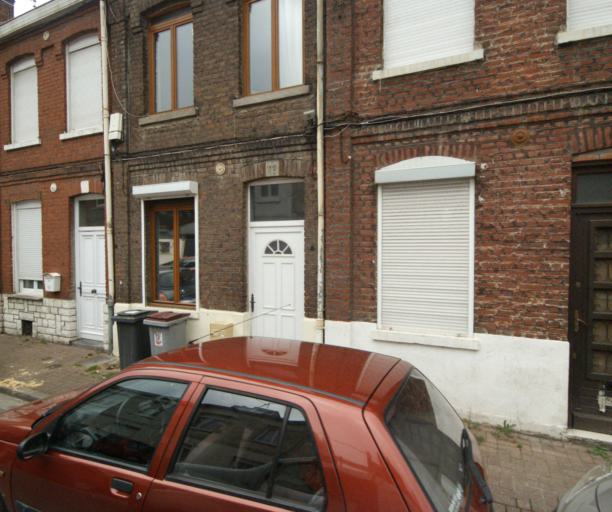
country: FR
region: Nord-Pas-de-Calais
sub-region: Departement du Nord
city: Lille
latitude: 50.6191
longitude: 3.0757
